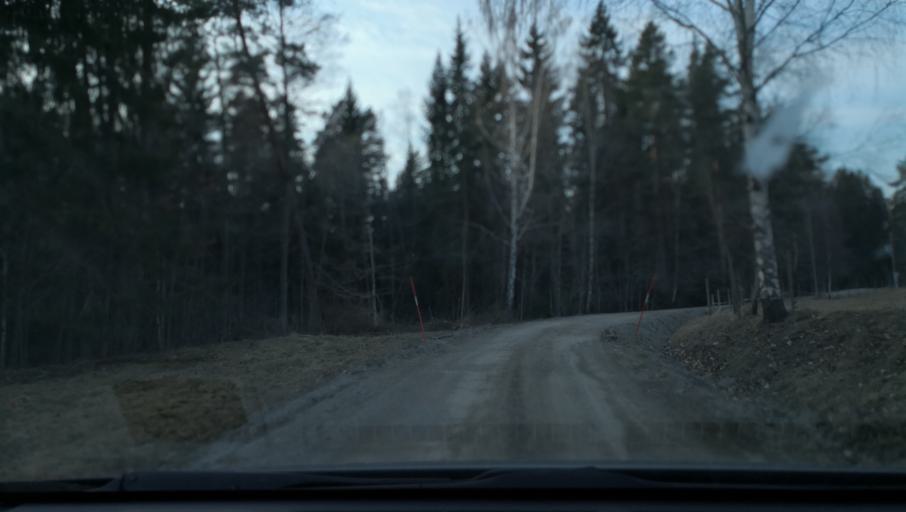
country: SE
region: OErebro
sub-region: Lindesbergs Kommun
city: Frovi
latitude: 59.3504
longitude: 15.3425
